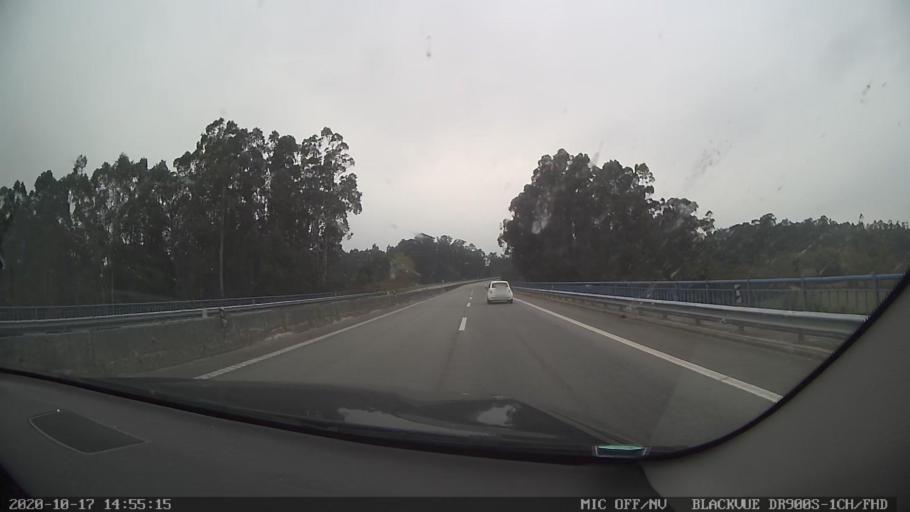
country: PT
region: Braga
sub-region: Esposende
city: Apulia
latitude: 41.4924
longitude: -8.7107
